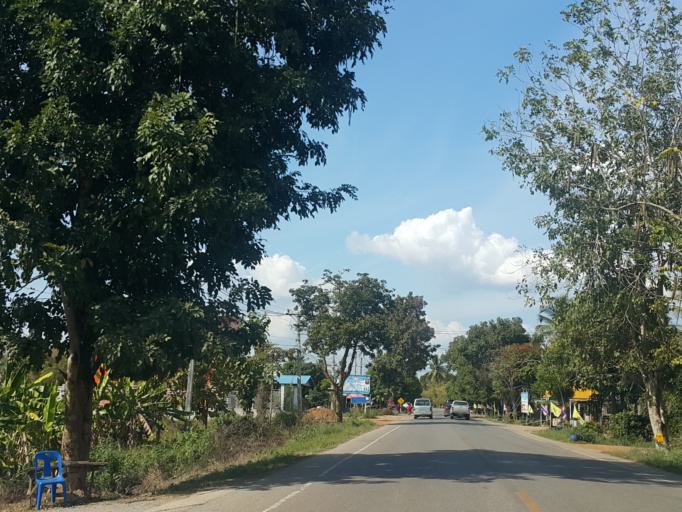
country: TH
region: Sukhothai
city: Sawankhalok
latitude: 17.2903
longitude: 99.8324
